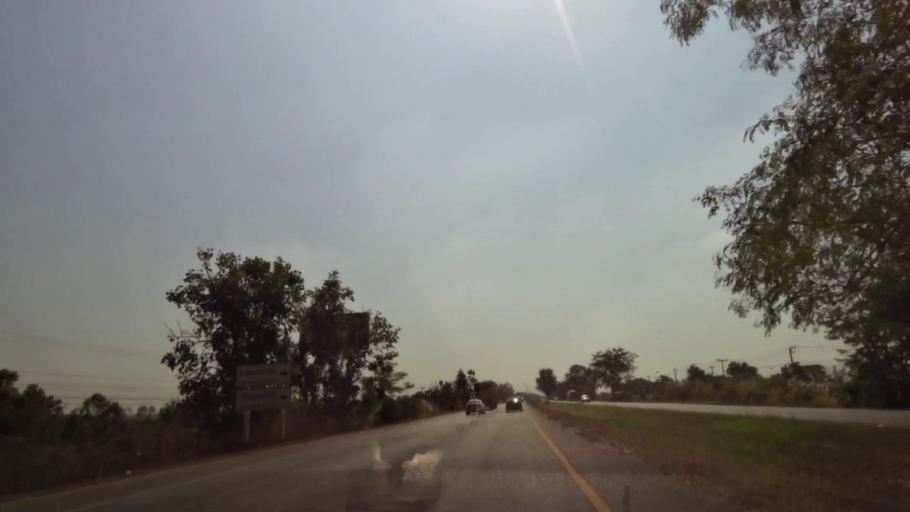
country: TH
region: Phichit
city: Wachira Barami
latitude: 16.4657
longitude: 100.1473
